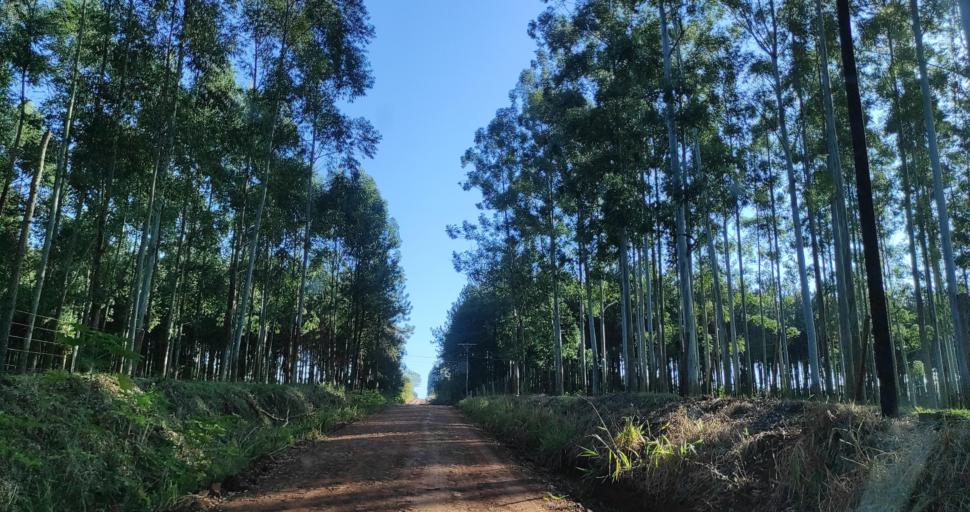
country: AR
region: Misiones
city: Puerto Rico
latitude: -26.8629
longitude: -55.0149
